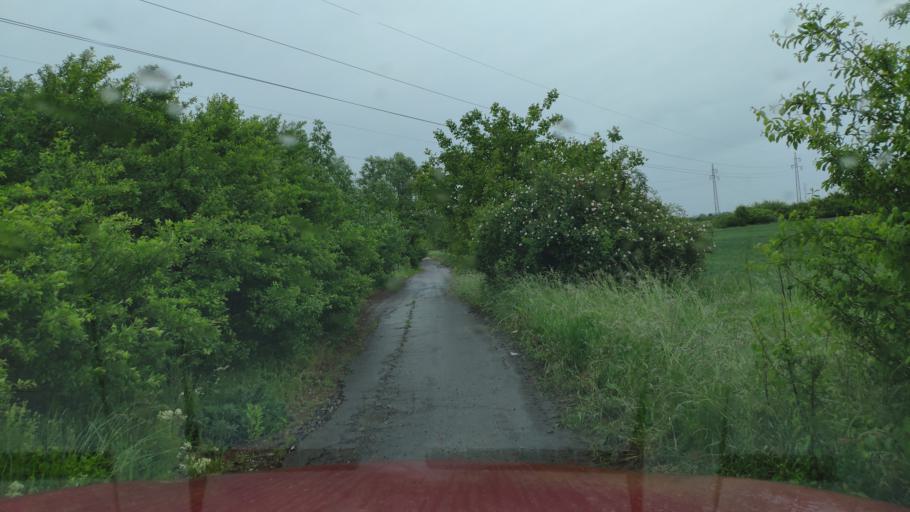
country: SK
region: Kosicky
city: Cierna nad Tisou
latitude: 48.4266
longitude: 22.0021
